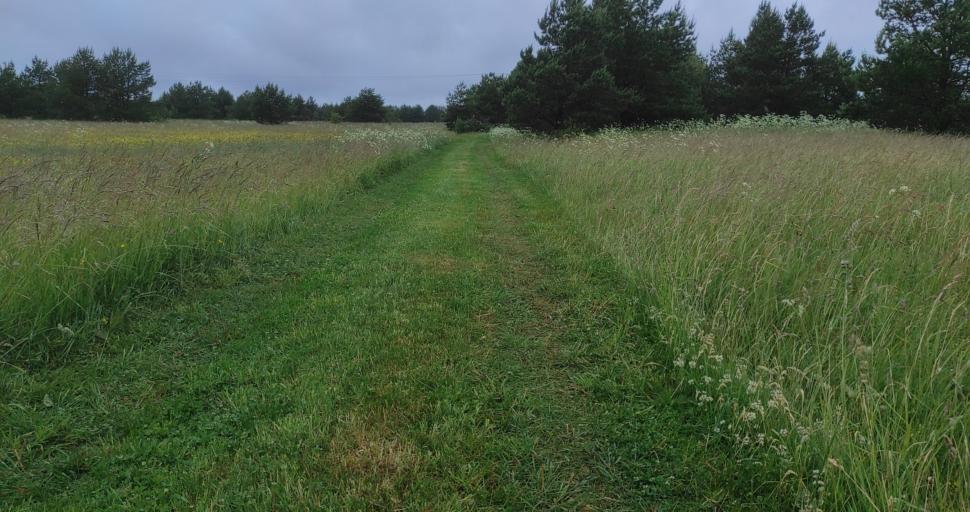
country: LV
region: Pavilostas
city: Pavilosta
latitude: 56.9556
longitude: 21.3164
